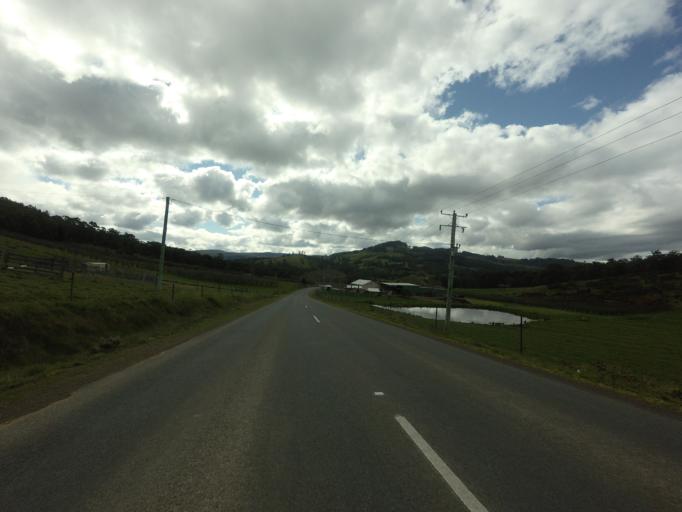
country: AU
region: Tasmania
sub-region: Huon Valley
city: Geeveston
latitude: -43.1748
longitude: 146.9463
